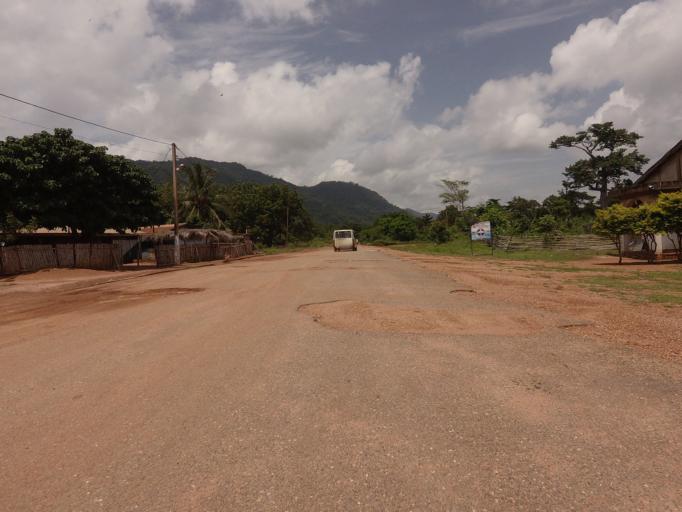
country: GH
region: Volta
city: Kpandu
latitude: 6.8131
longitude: 0.3747
